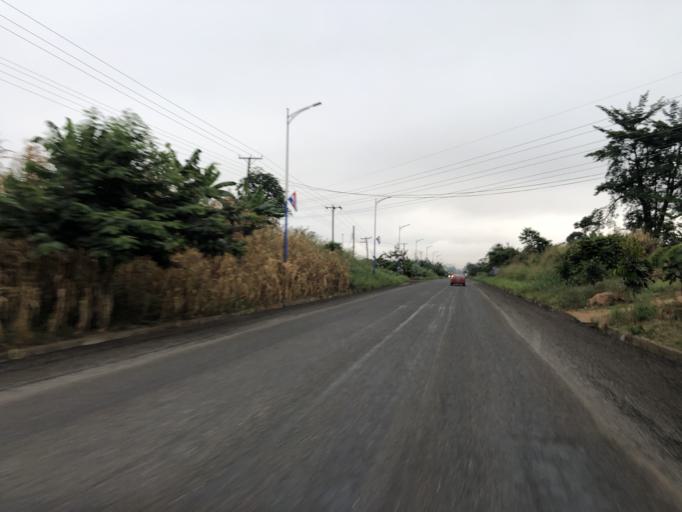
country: GH
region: Eastern
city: Koforidua
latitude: 6.1882
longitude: -0.3548
